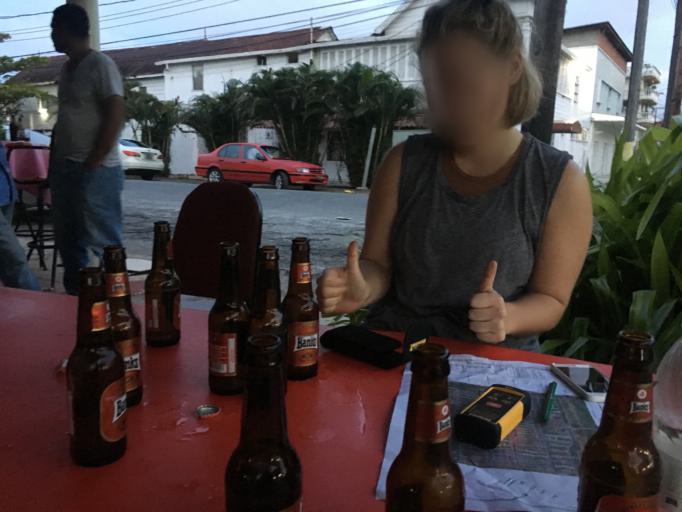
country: GY
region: Demerara-Mahaica
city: Georgetown
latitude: 6.8118
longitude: -58.1529
